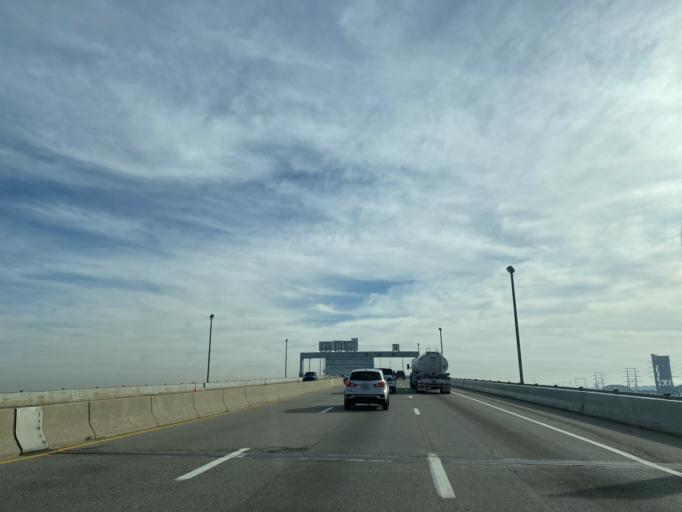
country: US
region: New Jersey
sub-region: Camden County
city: Pennsauken
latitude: 39.9876
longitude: -75.0722
